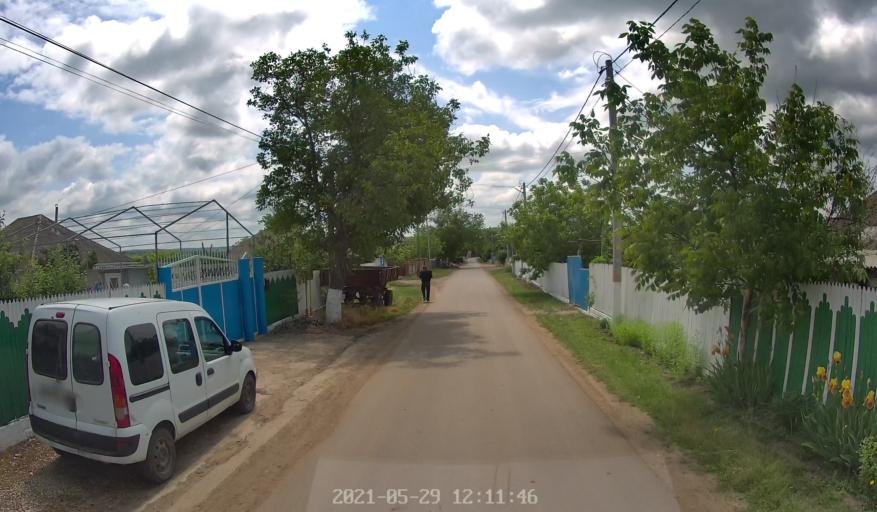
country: MD
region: Hincesti
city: Hincesti
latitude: 46.8819
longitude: 28.6305
